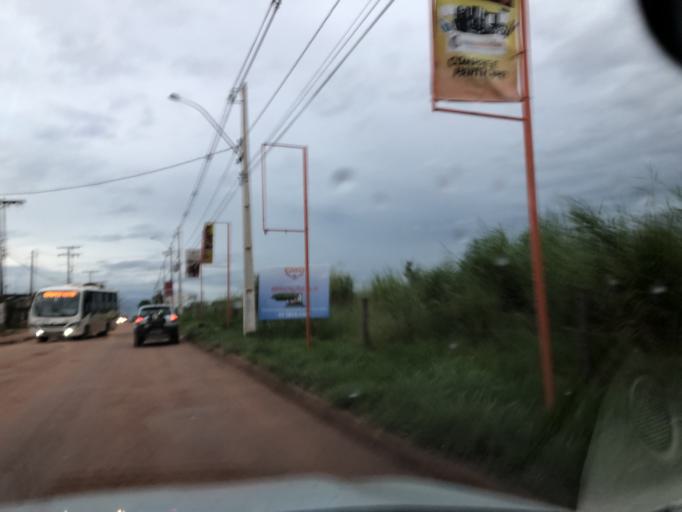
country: BR
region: Goias
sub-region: Luziania
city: Luziania
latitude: -16.1070
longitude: -47.9758
